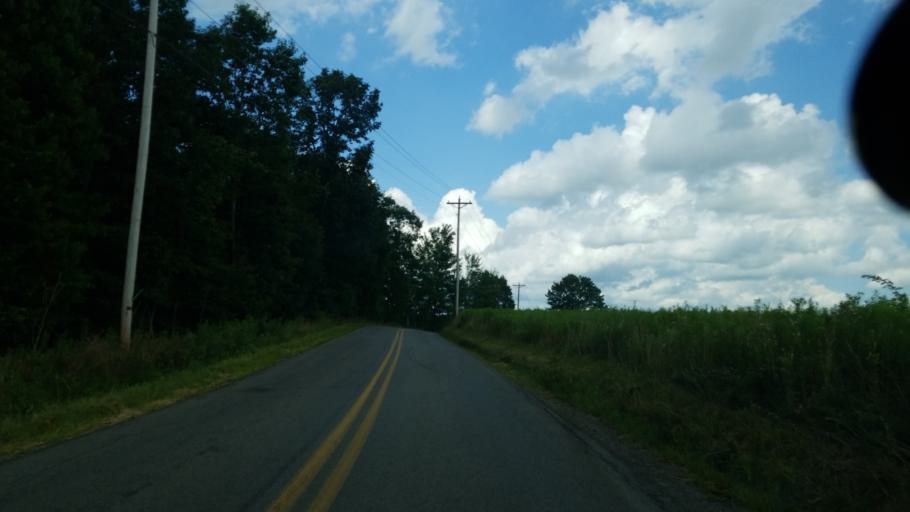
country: US
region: Pennsylvania
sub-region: Jefferson County
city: Brookville
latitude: 41.2322
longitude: -79.0829
